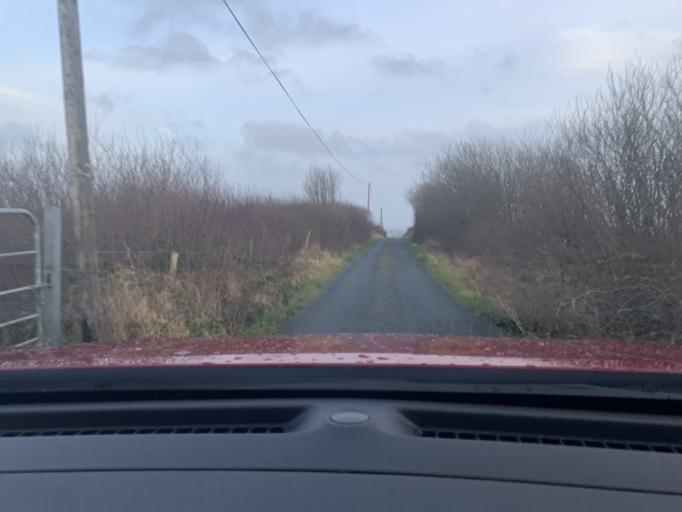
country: IE
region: Connaught
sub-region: Roscommon
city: Ballaghaderreen
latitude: 53.9473
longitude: -8.5079
